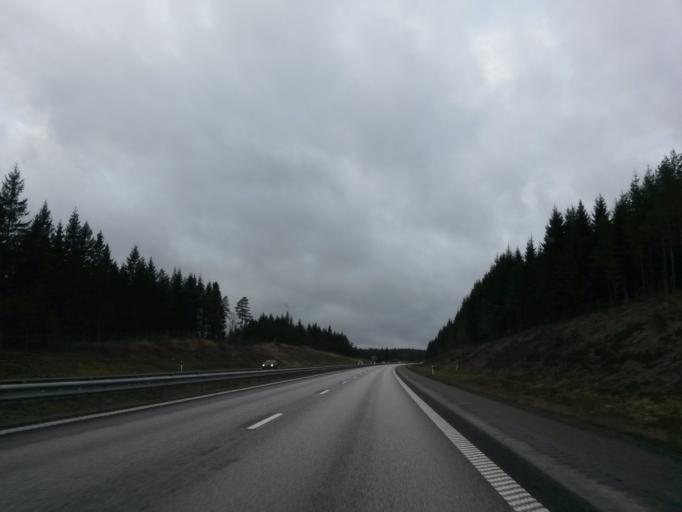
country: SE
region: Vaestra Goetaland
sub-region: Harryda Kommun
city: Hindas
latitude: 57.6672
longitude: 12.3970
